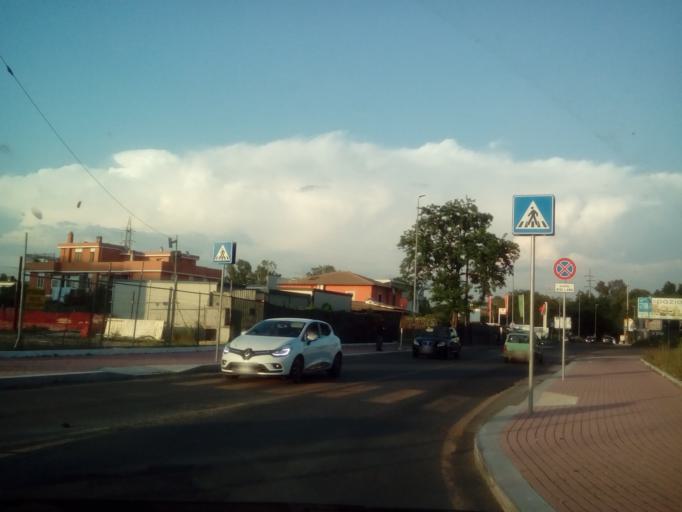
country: IT
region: Latium
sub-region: Citta metropolitana di Roma Capitale
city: Setteville
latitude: 41.9049
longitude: 12.5979
